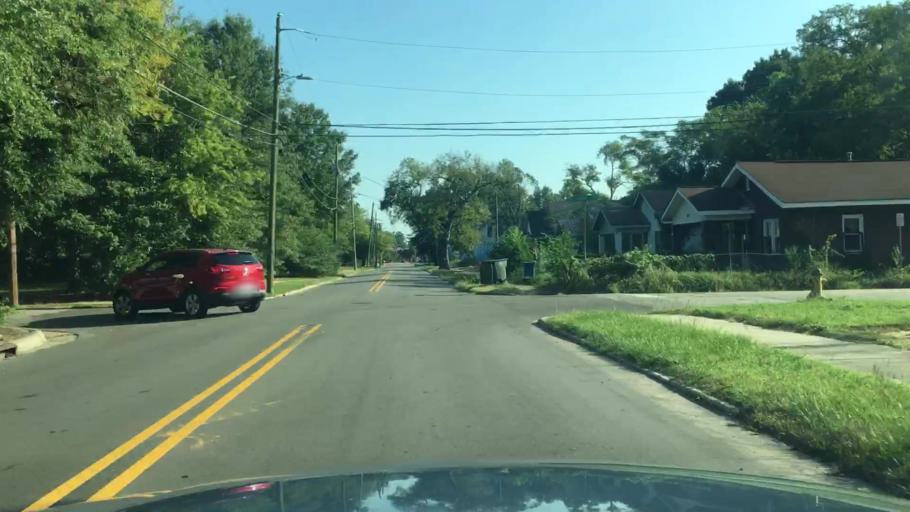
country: US
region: North Carolina
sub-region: Cumberland County
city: Fayetteville
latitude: 35.0460
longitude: -78.8770
